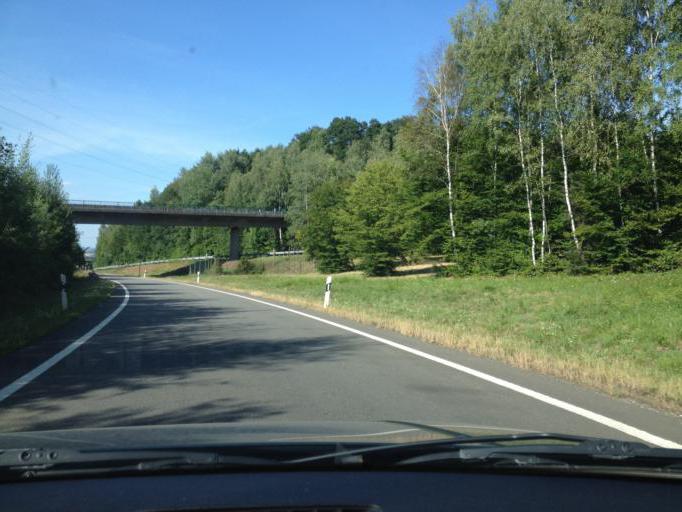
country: DE
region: Saarland
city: Spiesen-Elversberg
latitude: 49.3245
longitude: 7.1583
